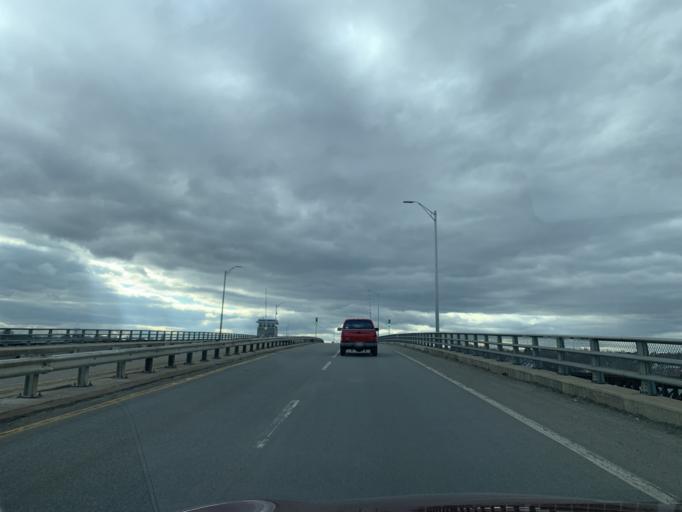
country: US
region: Massachusetts
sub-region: Essex County
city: Newburyport
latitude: 42.8172
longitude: -70.8714
